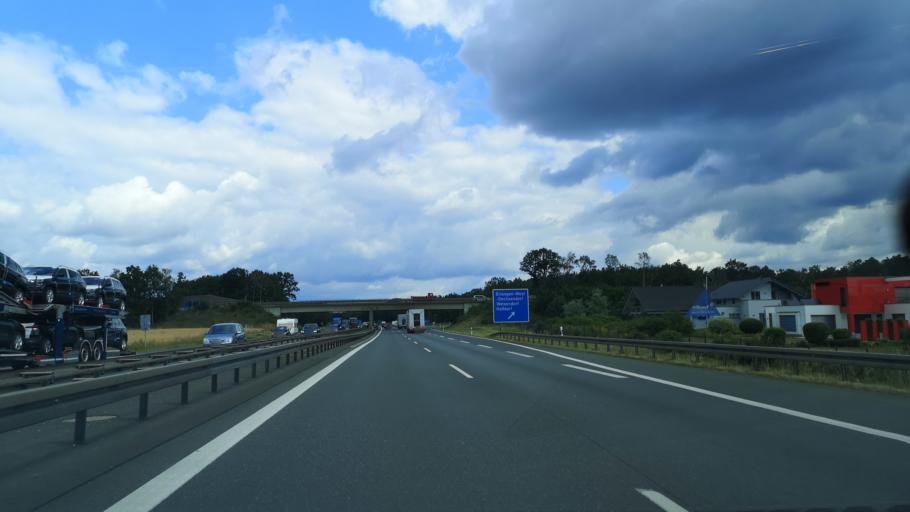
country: DE
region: Bavaria
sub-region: Regierungsbezirk Mittelfranken
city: Hessdorf
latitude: 49.6269
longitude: 10.9189
